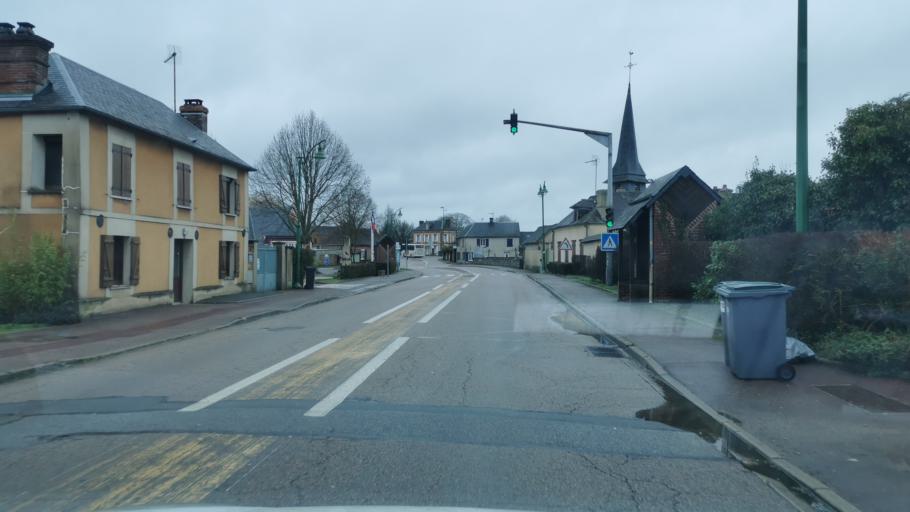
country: FR
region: Haute-Normandie
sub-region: Departement de l'Eure
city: Normanville
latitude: 49.0811
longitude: 1.1810
